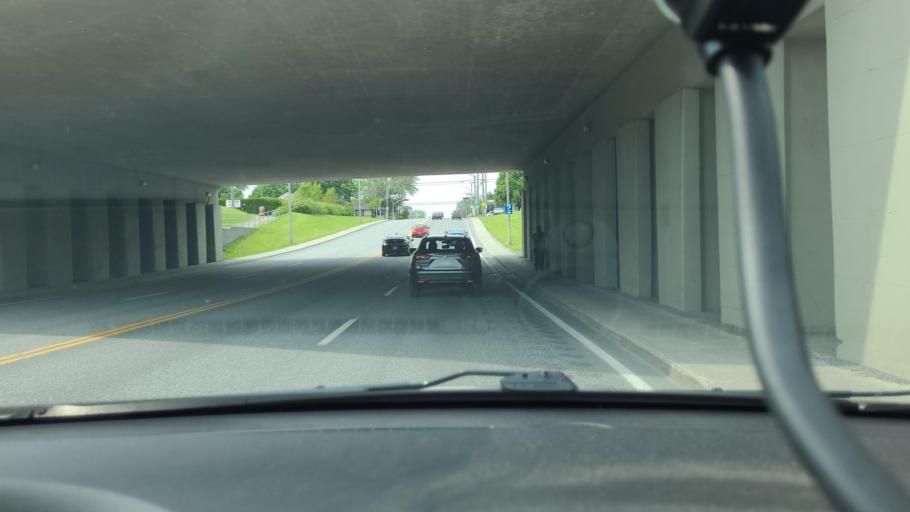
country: CA
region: Quebec
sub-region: Monteregie
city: Saint-Hyacinthe
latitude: 45.6247
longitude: -72.9616
